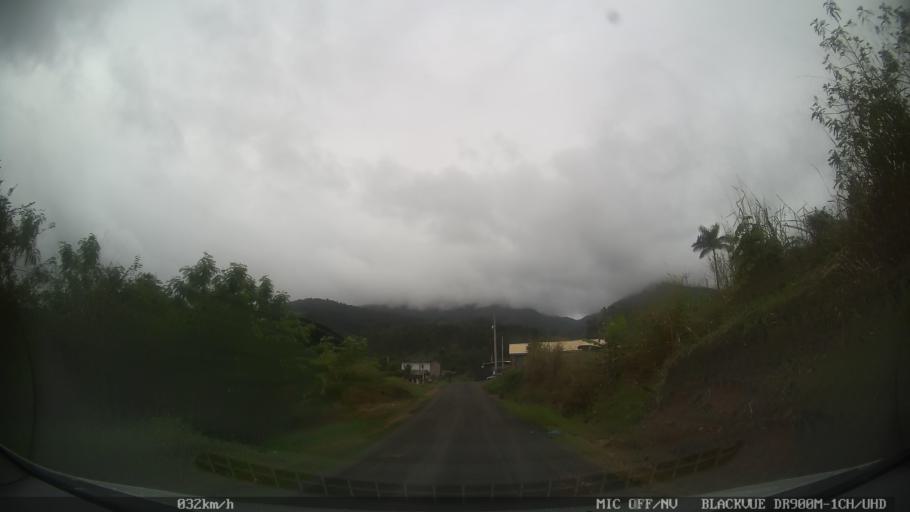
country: BR
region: Sao Paulo
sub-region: Cajati
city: Cajati
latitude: -24.7893
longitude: -48.1779
